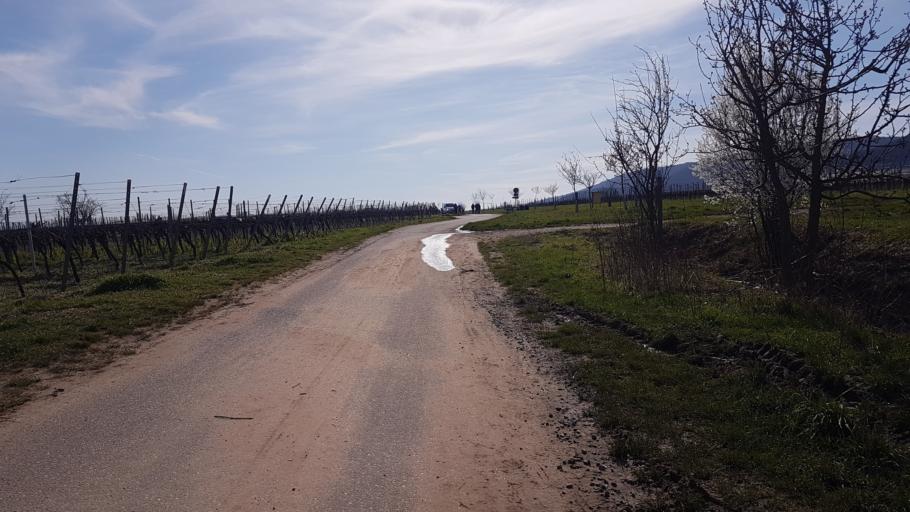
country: DE
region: Rheinland-Pfalz
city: Maikammer
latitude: 49.3195
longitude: 8.1304
